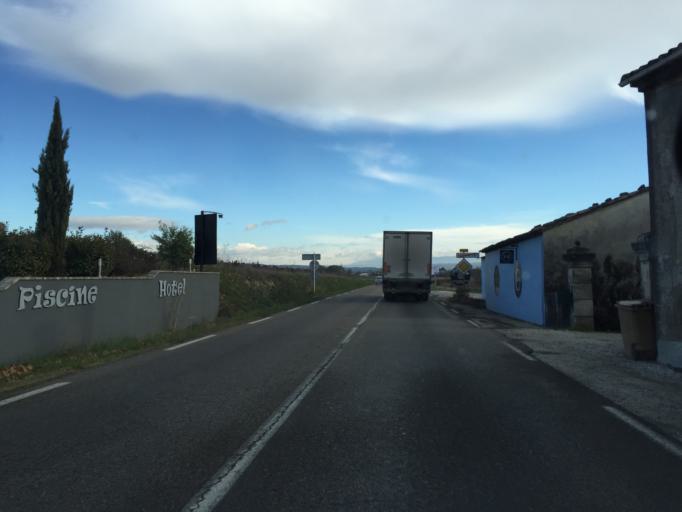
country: FR
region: Provence-Alpes-Cote d'Azur
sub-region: Departement du Vaucluse
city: Maubec
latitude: 43.8679
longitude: 5.1490
